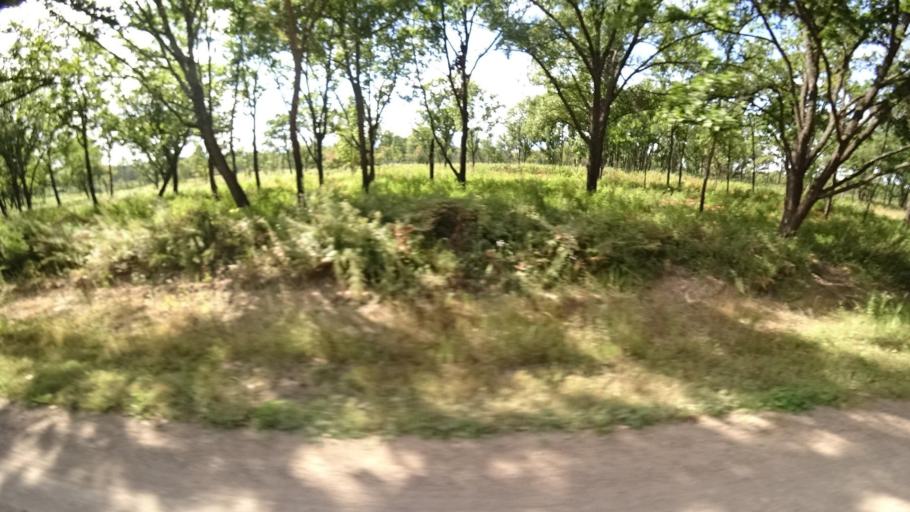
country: RU
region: Primorskiy
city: Yakovlevka
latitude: 44.3988
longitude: 133.5618
